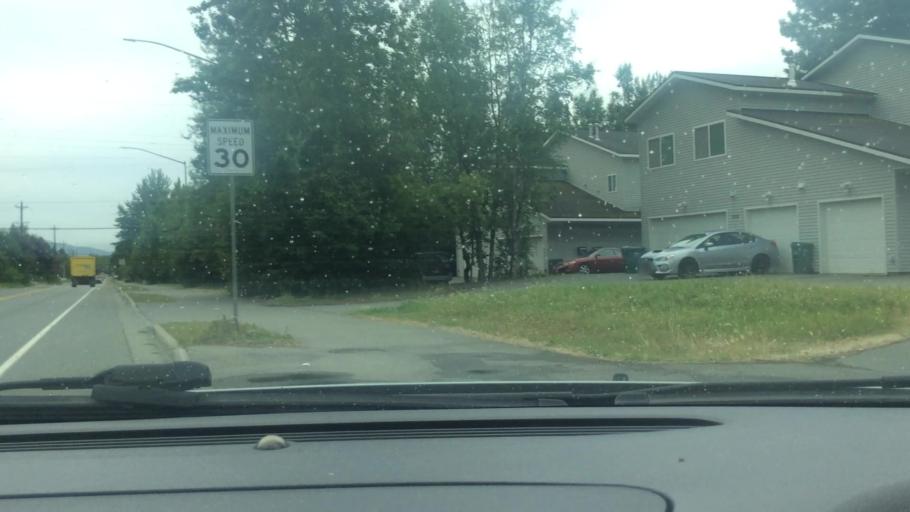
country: US
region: Alaska
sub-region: Anchorage Municipality
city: Elmendorf Air Force Base
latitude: 61.2178
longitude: -149.7561
